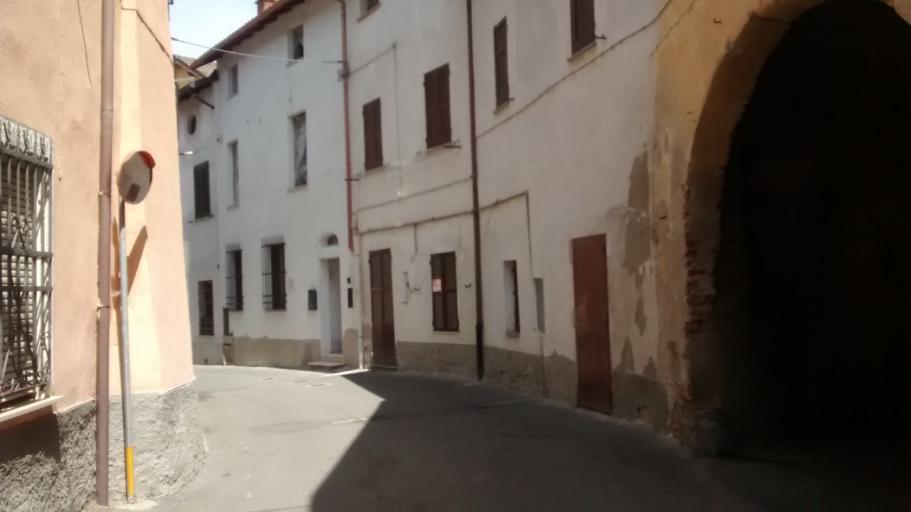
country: IT
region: Piedmont
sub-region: Provincia di Alessandria
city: Capriata d'Orba
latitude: 44.7313
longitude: 8.6896
